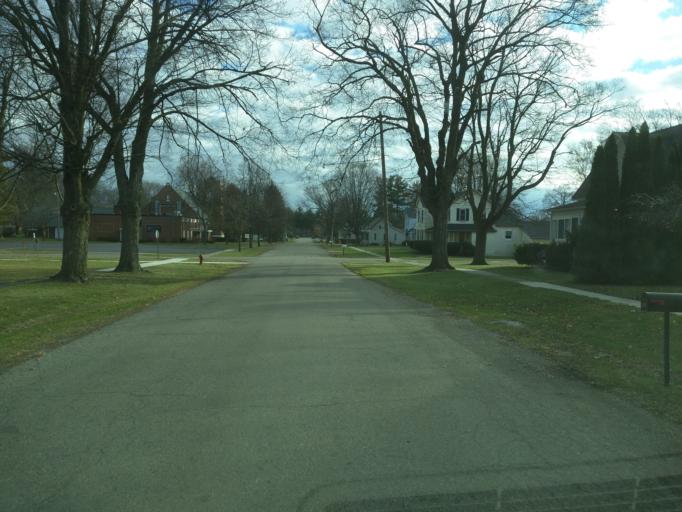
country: US
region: Michigan
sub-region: Livingston County
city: Fowlerville
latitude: 42.6596
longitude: -84.0683
